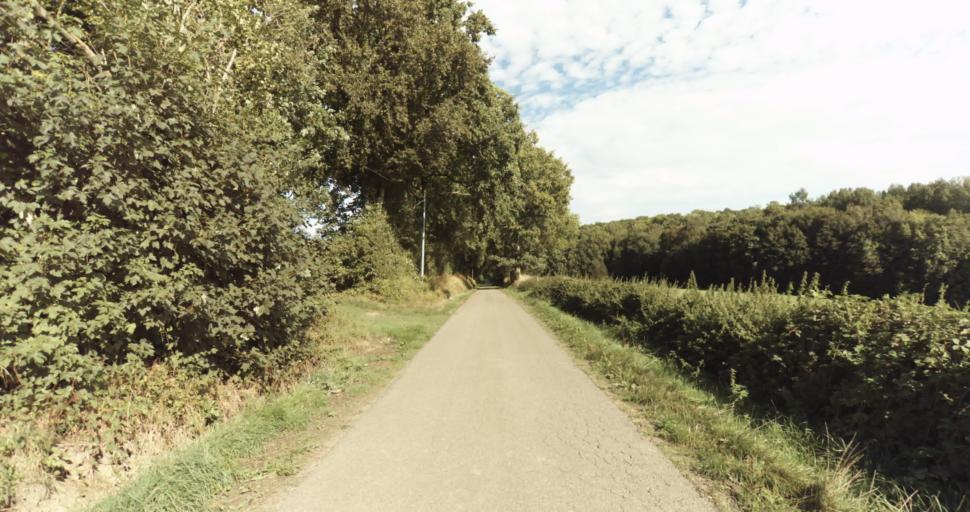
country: FR
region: Lower Normandy
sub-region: Departement de l'Orne
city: Gace
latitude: 48.8071
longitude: 0.2269
